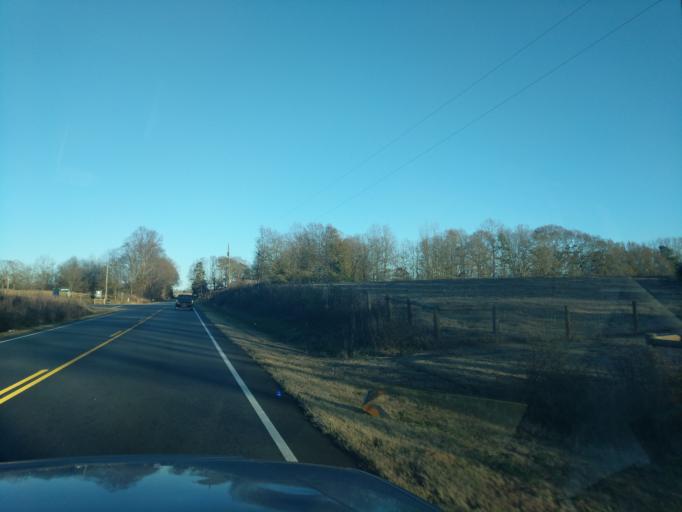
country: US
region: South Carolina
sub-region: Oconee County
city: Utica
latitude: 34.5842
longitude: -82.9343
